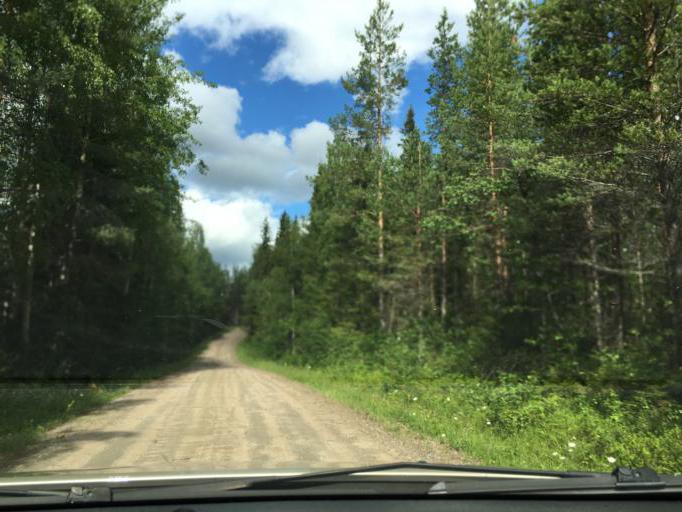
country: SE
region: Norrbotten
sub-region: Overkalix Kommun
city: OEverkalix
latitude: 66.1321
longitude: 22.7844
